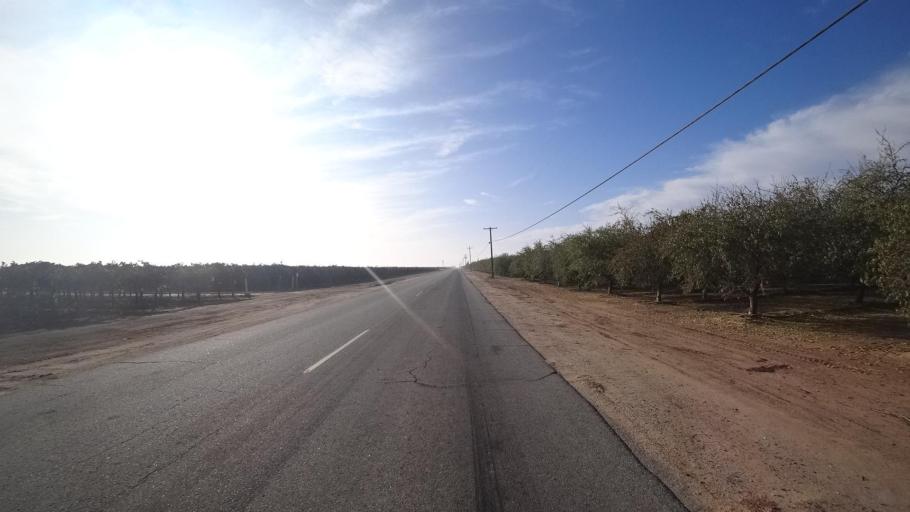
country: US
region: California
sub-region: Kern County
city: McFarland
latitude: 35.6708
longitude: -119.2047
